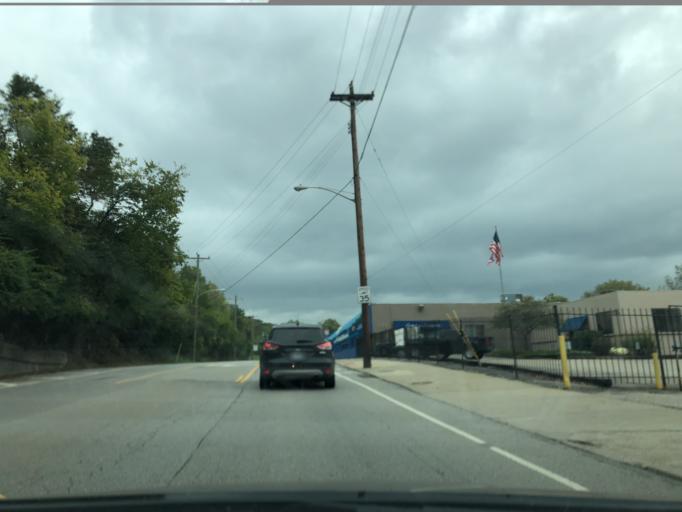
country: US
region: Kentucky
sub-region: Campbell County
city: Bellevue
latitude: 39.1170
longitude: -84.4841
